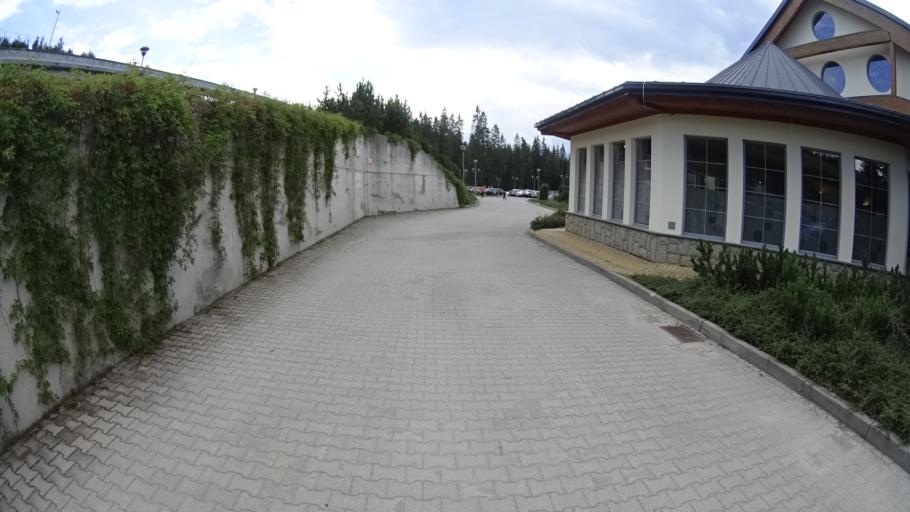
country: PL
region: Lesser Poland Voivodeship
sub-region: Powiat tatrzanski
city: Bukowina Tatrzanska
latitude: 49.3256
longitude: 20.0945
